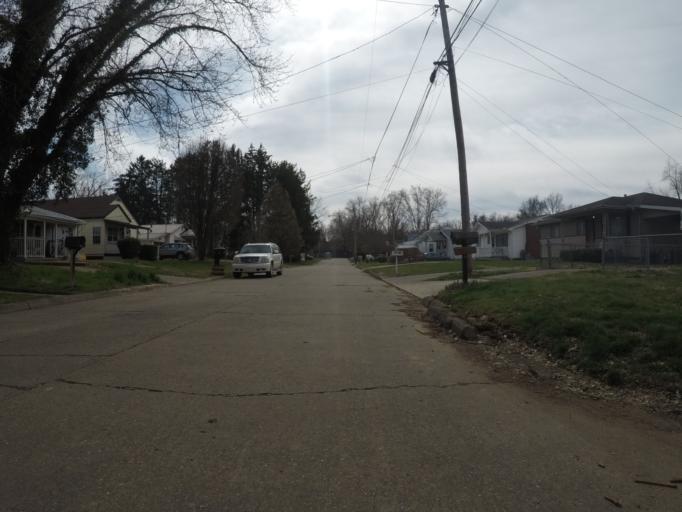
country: US
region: West Virginia
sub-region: Cabell County
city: Pea Ridge
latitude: 38.4147
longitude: -82.3662
